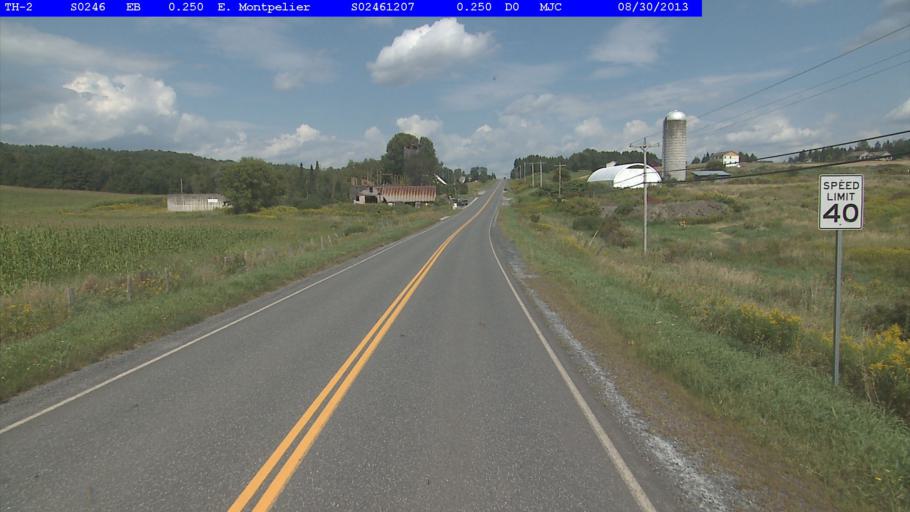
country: US
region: Vermont
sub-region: Washington County
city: Montpelier
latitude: 44.2560
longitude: -72.5180
